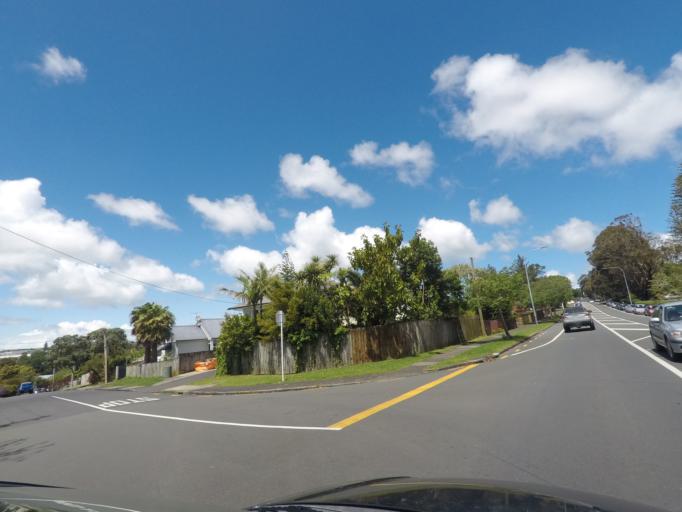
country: NZ
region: Auckland
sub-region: Auckland
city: Waitakere
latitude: -36.9035
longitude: 174.6544
